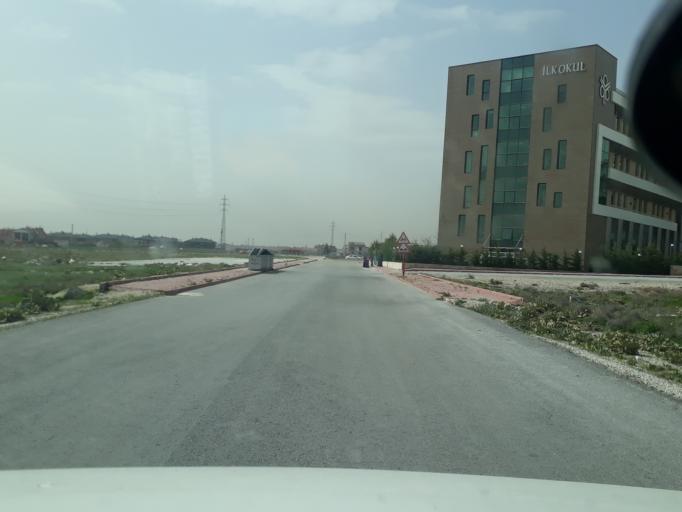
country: TR
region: Konya
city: Sille
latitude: 37.9467
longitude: 32.4756
